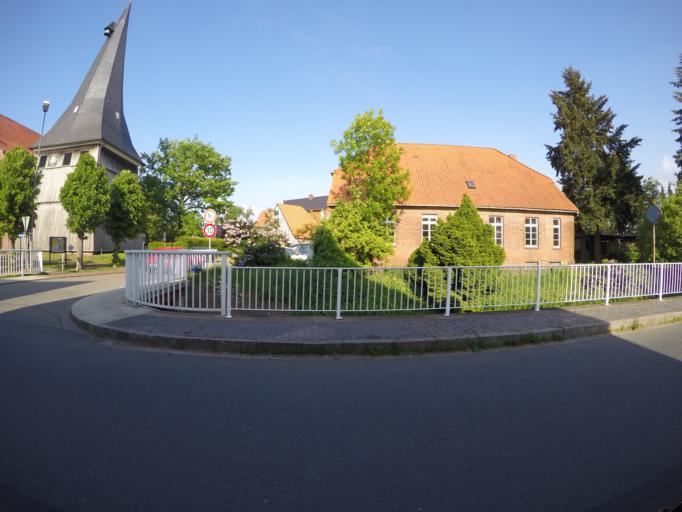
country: DE
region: Lower Saxony
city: Nottensdorf
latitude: 53.4857
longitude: 9.6442
